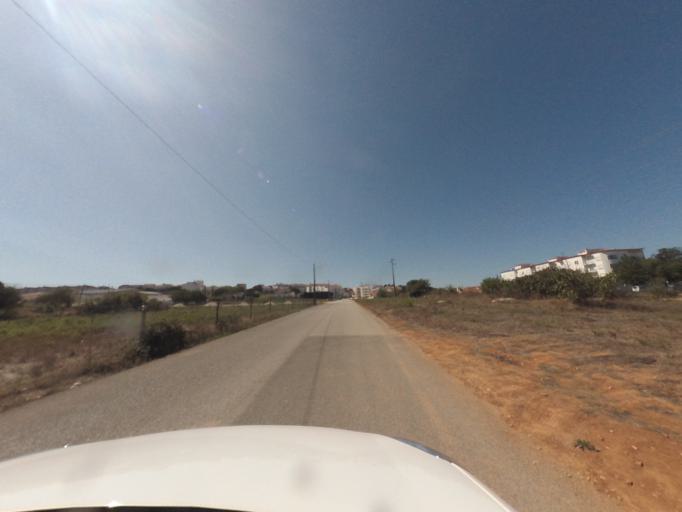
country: PT
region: Leiria
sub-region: Alcobaca
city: Turquel
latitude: 39.4636
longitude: -8.9733
